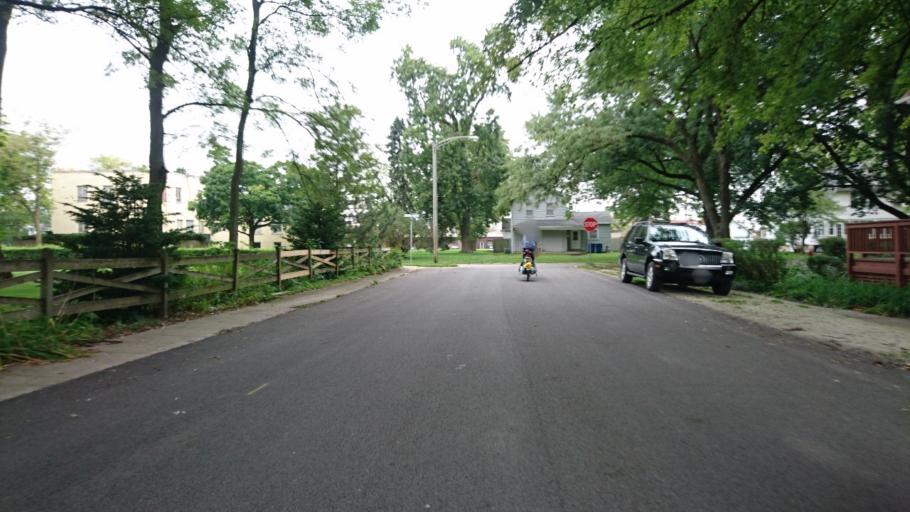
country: US
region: Illinois
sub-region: Livingston County
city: Dwight
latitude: 41.0901
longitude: -88.4280
